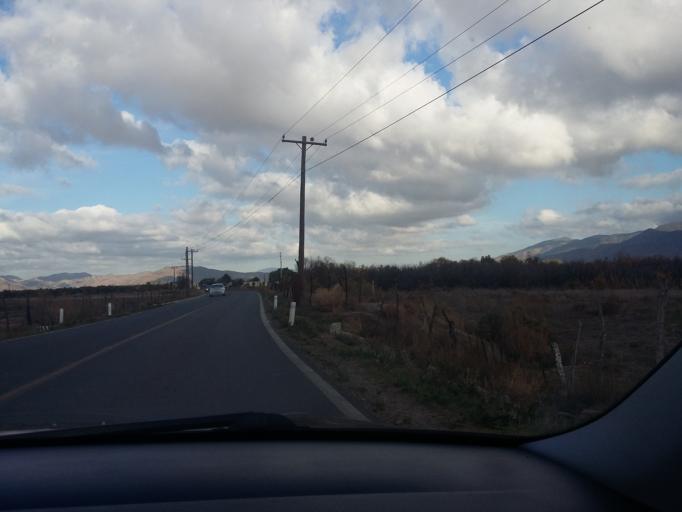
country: MX
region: Baja California
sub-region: Ensenada
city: Rancho Verde
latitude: 32.0633
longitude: -116.6435
